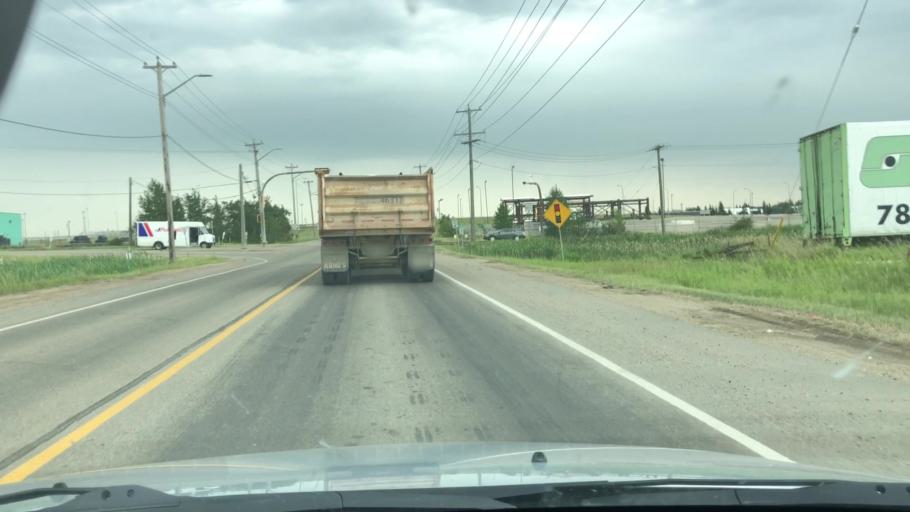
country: CA
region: Alberta
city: Sherwood Park
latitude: 53.5202
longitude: -113.3939
